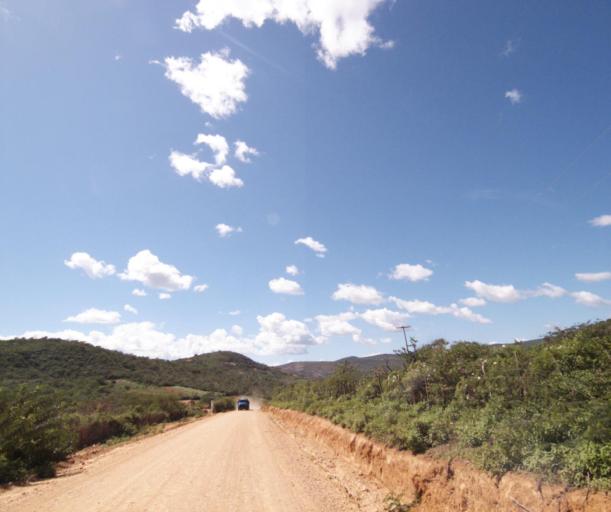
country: BR
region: Bahia
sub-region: Pocoes
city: Pocoes
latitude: -14.2677
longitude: -40.6962
